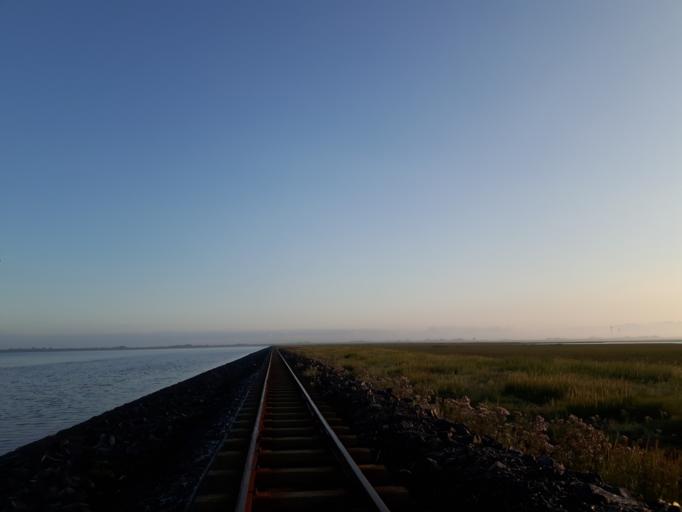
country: DE
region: Schleswig-Holstein
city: Dagebull
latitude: 54.7010
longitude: 8.7108
